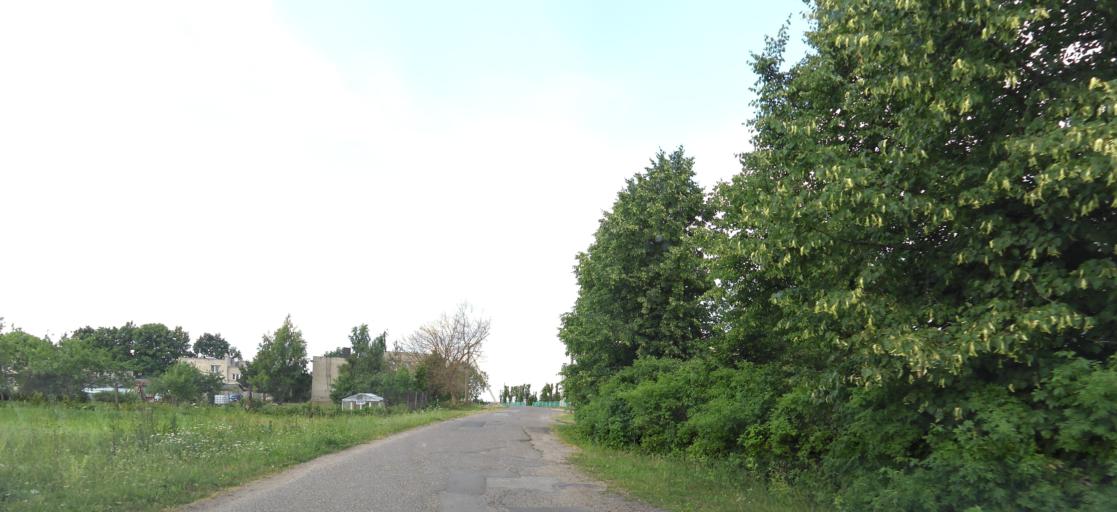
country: LT
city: Skaidiskes
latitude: 54.5358
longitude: 25.6507
